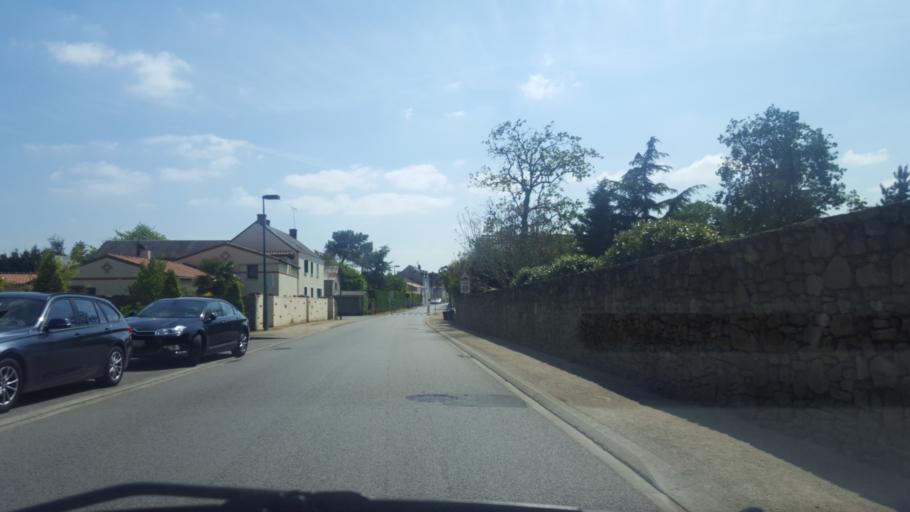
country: FR
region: Pays de la Loire
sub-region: Departement de la Loire-Atlantique
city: La Limouziniere
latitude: 46.9681
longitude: -1.5760
